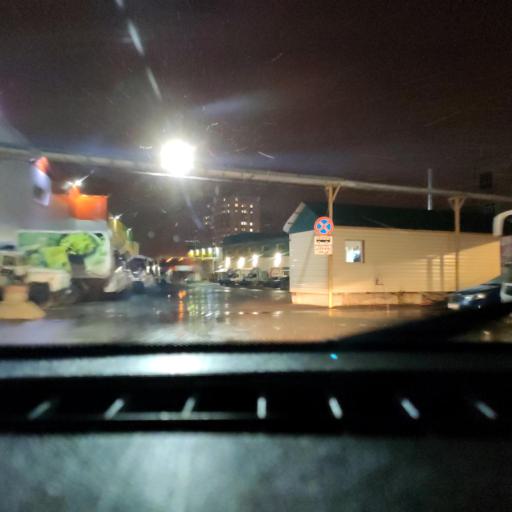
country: RU
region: Bashkortostan
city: Ufa
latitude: 54.7730
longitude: 56.1219
